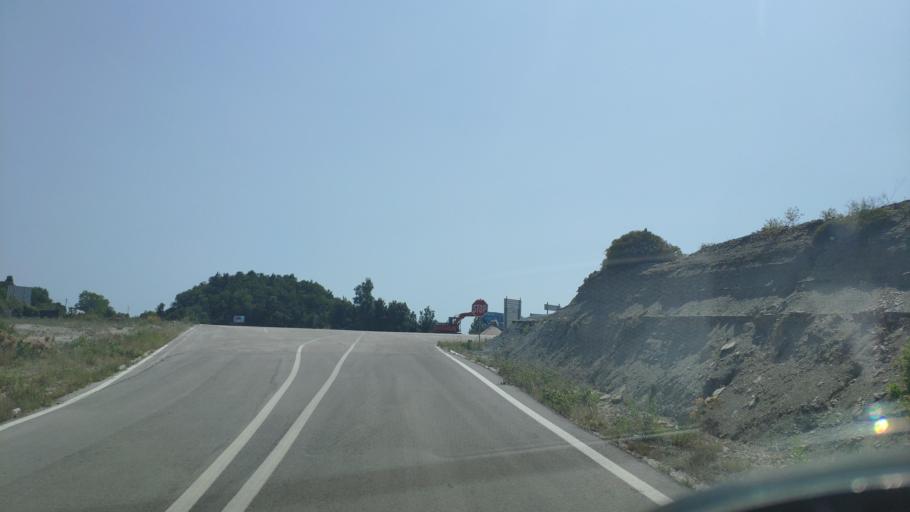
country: GR
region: Epirus
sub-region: Nomos Artas
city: Ano Kalentini
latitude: 39.2153
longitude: 21.1180
